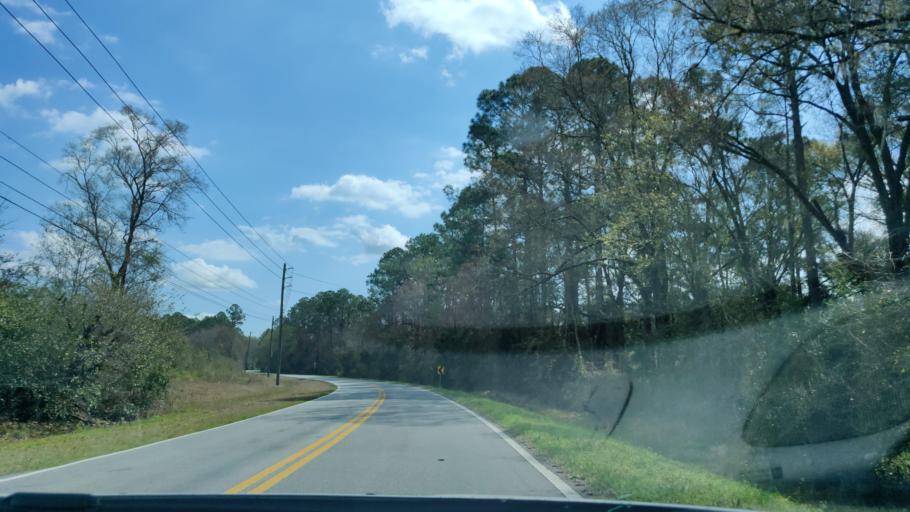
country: US
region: Florida
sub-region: Duval County
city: Baldwin
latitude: 30.2460
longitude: -81.9476
